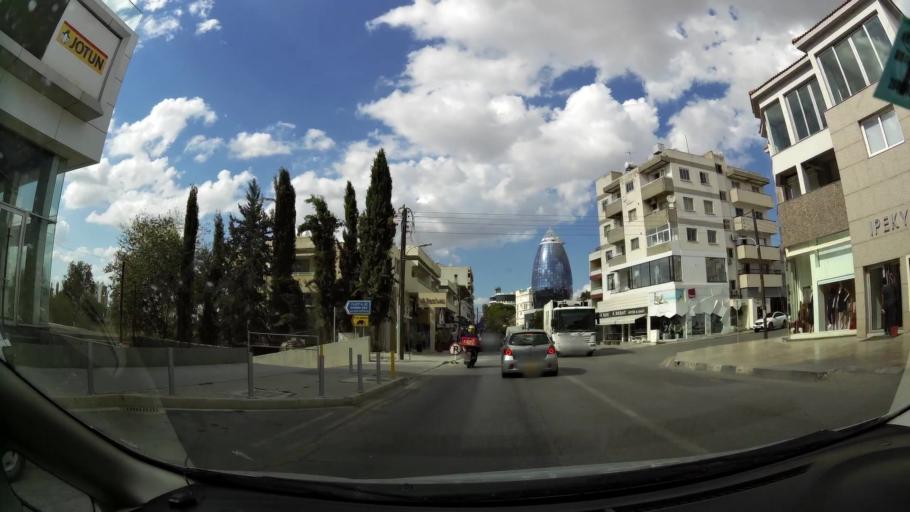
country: CY
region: Lefkosia
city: Nicosia
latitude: 35.1893
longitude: 33.3495
